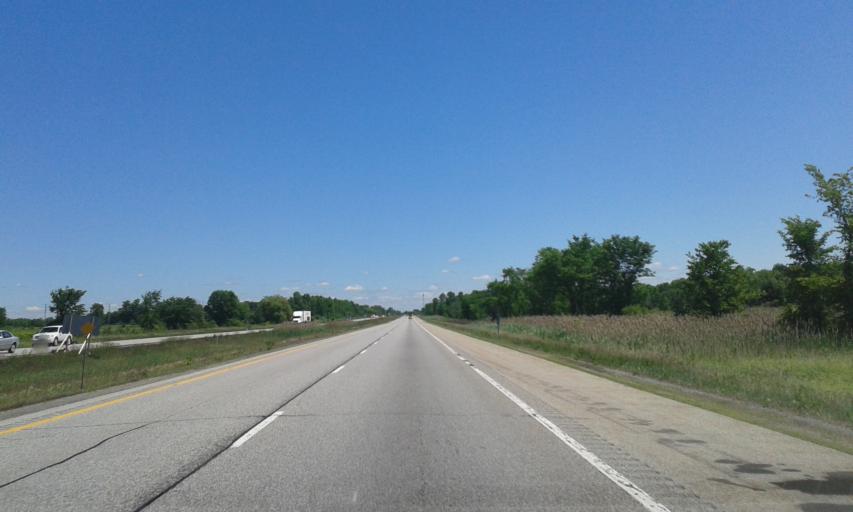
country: US
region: New York
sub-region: St. Lawrence County
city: Ogdensburg
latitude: 44.8790
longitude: -75.2879
